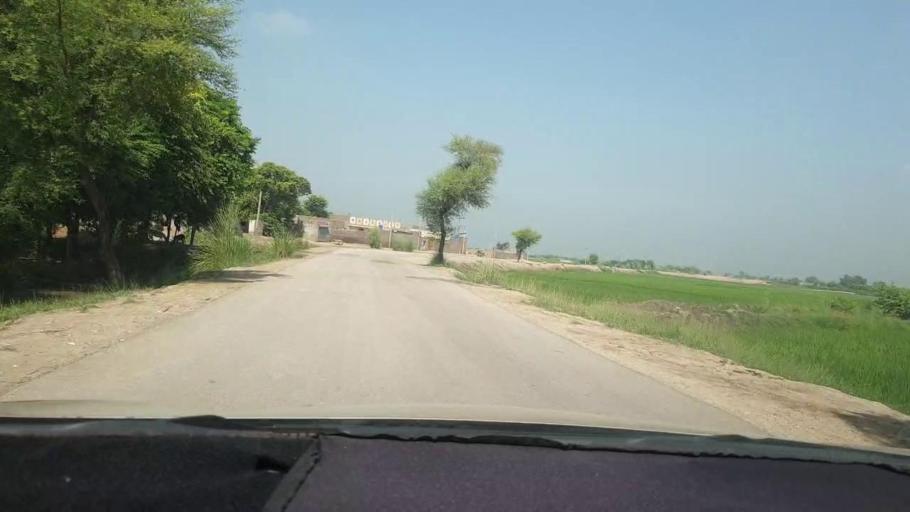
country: PK
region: Sindh
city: Miro Khan
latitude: 27.7727
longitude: 68.0595
